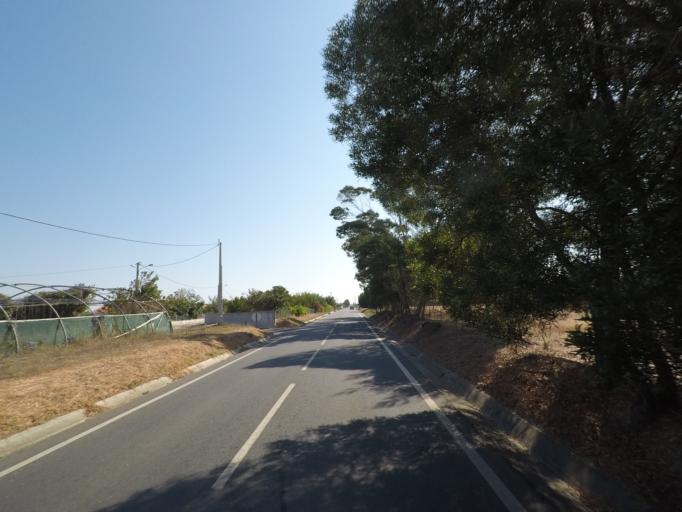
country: PT
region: Beja
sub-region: Odemira
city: Odemira
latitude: 37.5903
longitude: -8.6750
